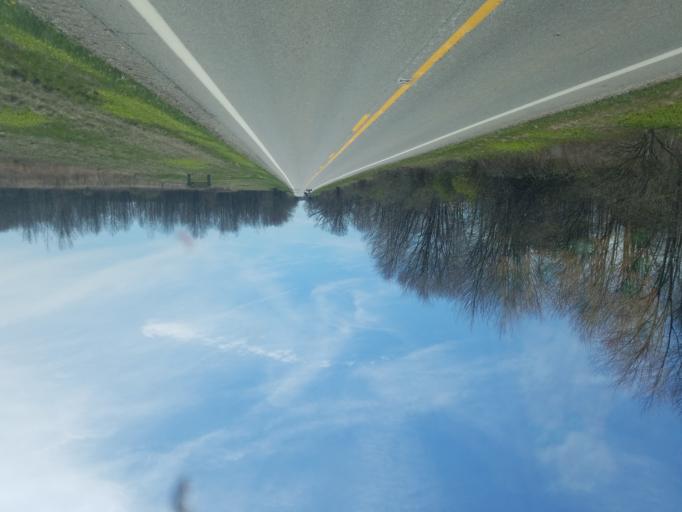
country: US
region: Ohio
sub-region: Delaware County
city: Ashley
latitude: 40.4320
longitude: -83.0457
